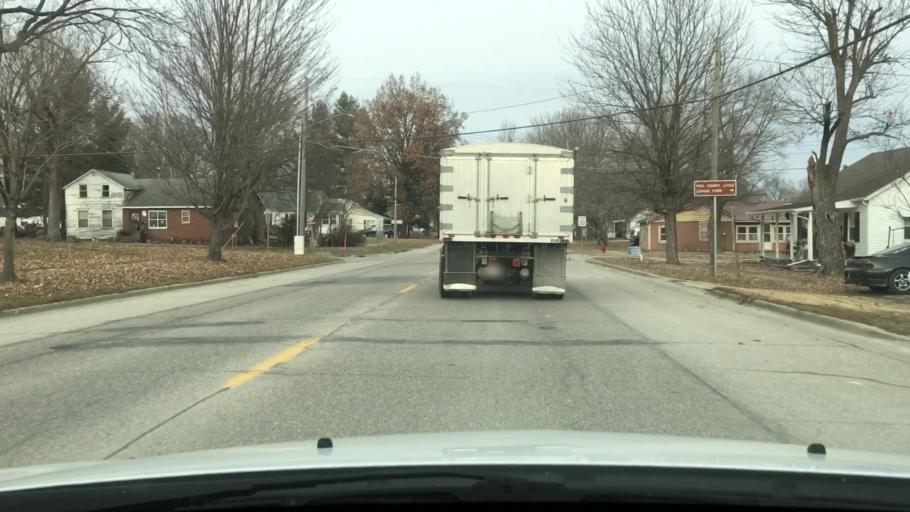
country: US
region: Illinois
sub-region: Pike County
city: Pittsfield
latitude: 39.6117
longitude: -90.8030
